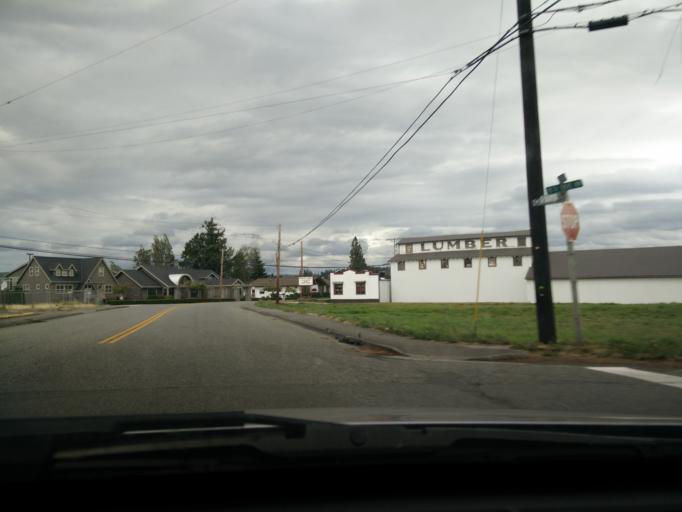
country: US
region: Washington
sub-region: Snohomish County
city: Stanwood
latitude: 48.2416
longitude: -122.3661
